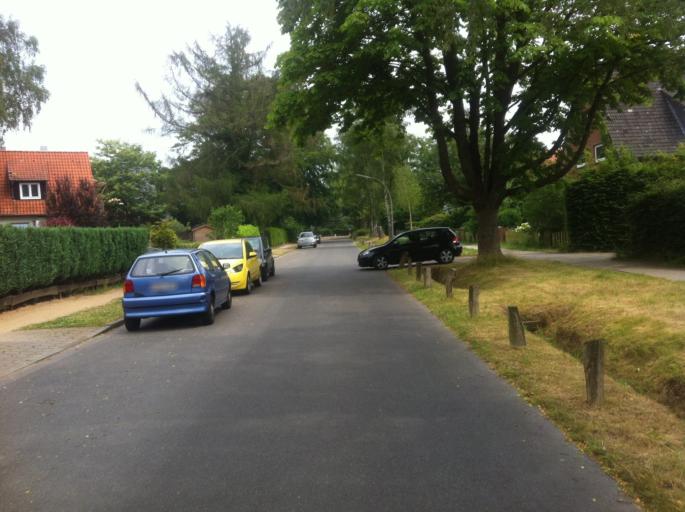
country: DE
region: Hamburg
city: Farmsen-Berne
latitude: 53.6270
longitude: 10.1414
